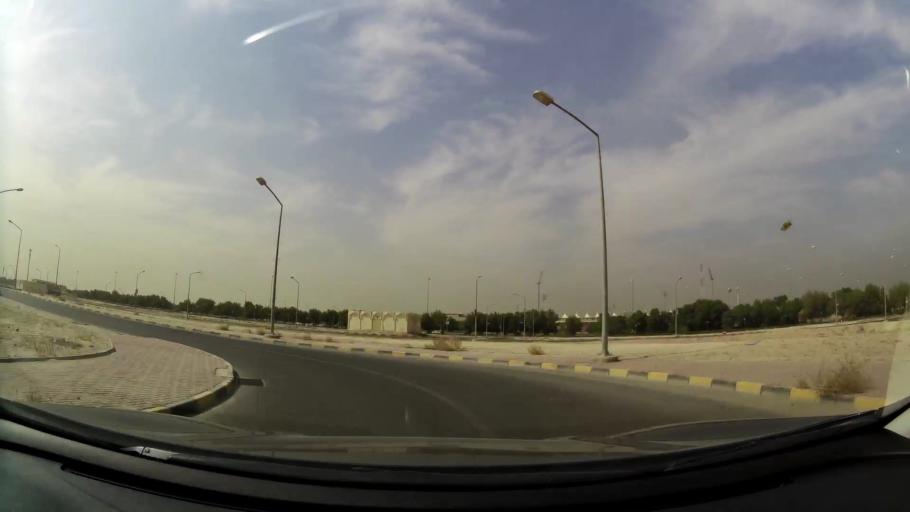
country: KW
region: Al Farwaniyah
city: Janub as Surrah
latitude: 29.2824
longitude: 47.9883
